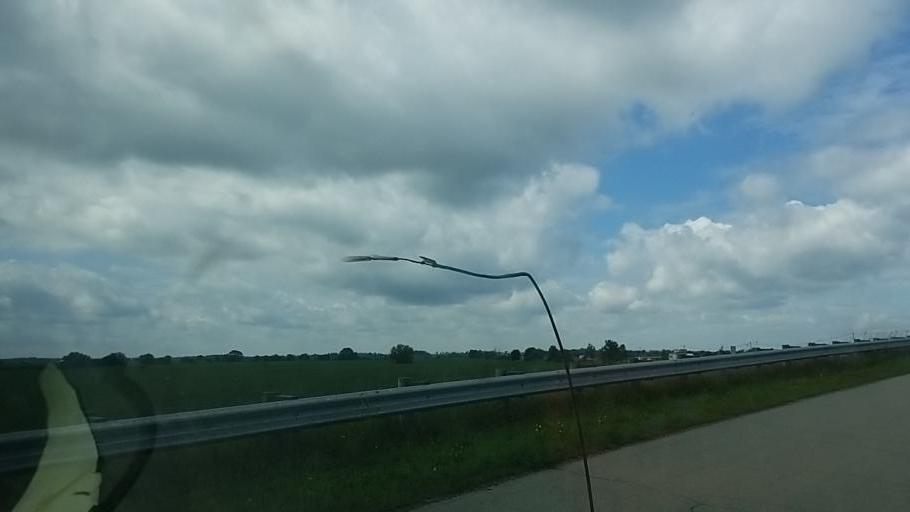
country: US
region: Ohio
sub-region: Fayette County
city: Jeffersonville
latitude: 39.6832
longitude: -83.4800
